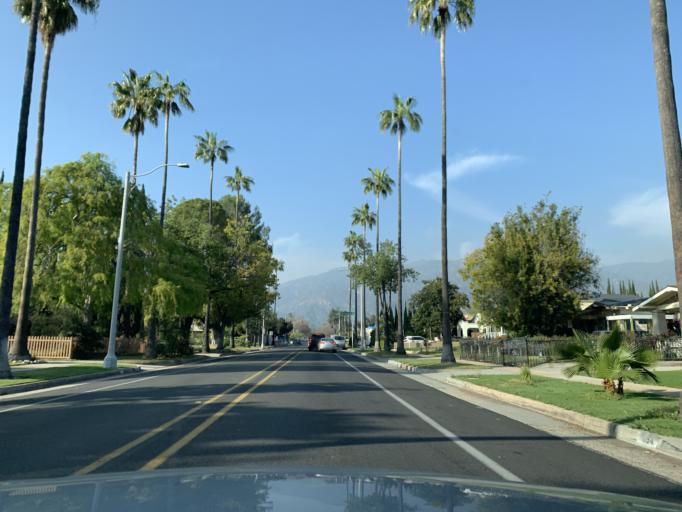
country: US
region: California
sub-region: Los Angeles County
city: Altadena
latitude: 34.1675
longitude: -118.1215
